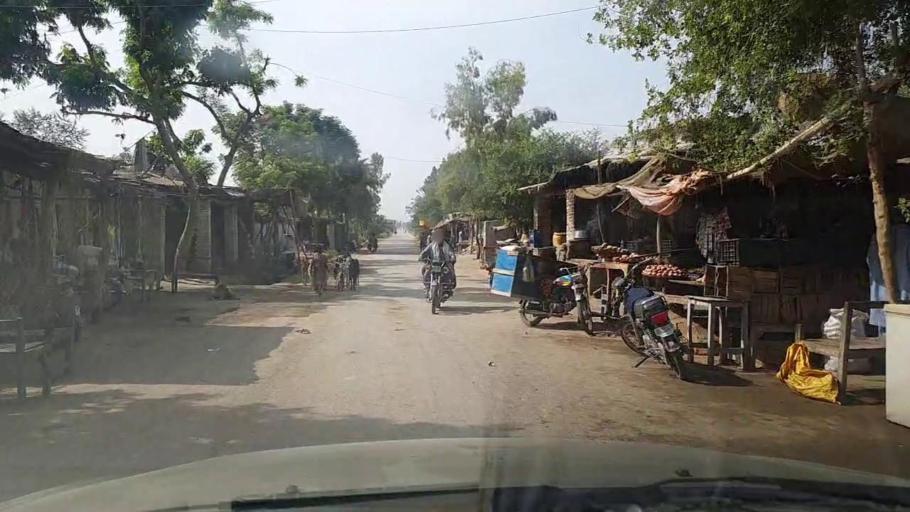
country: PK
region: Sindh
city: Gambat
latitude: 27.4512
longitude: 68.4861
